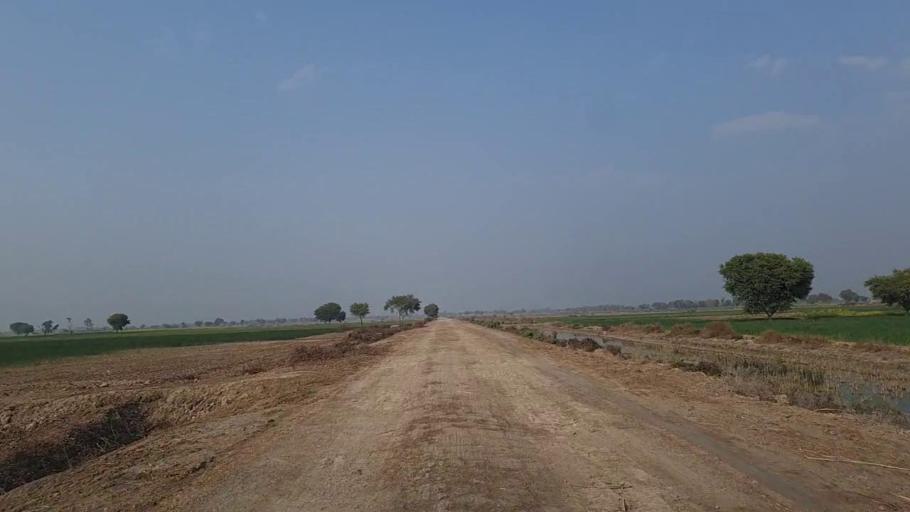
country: PK
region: Sindh
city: Nawabshah
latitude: 26.3372
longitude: 68.4737
